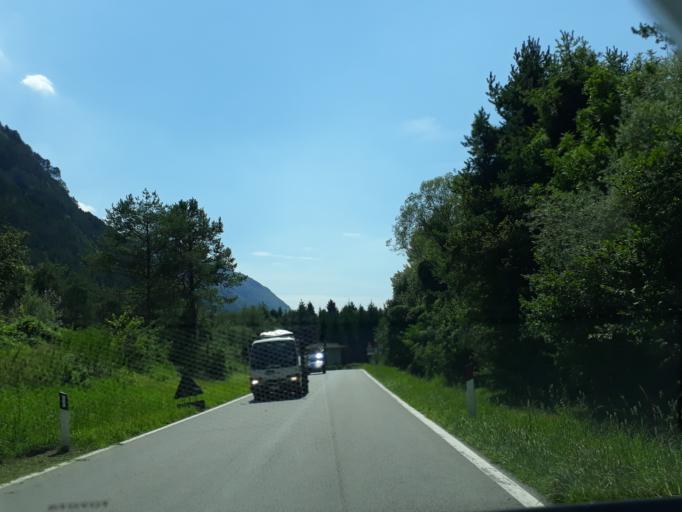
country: IT
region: Trentino-Alto Adige
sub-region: Provincia di Trento
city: Lodrone-Darzo
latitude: 45.8280
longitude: 10.5581
